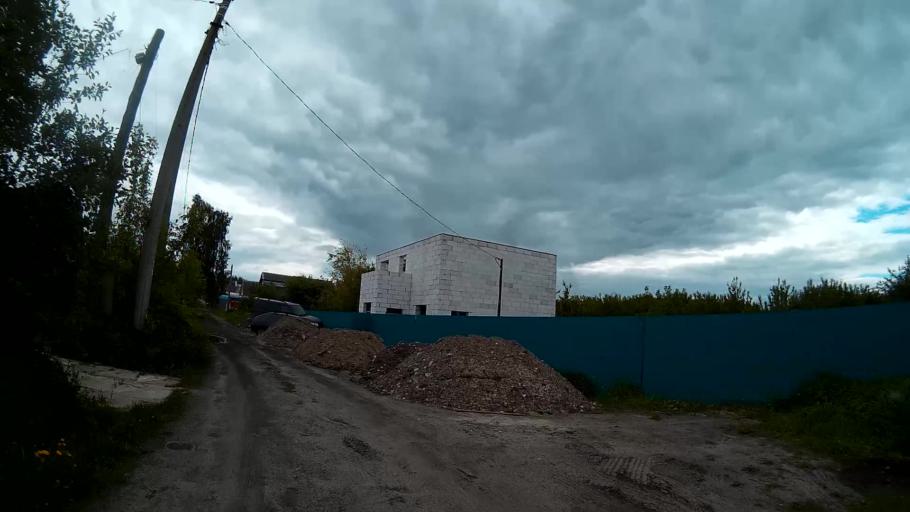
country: RU
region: Ulyanovsk
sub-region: Ulyanovskiy Rayon
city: Ulyanovsk
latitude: 54.2603
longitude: 48.3066
